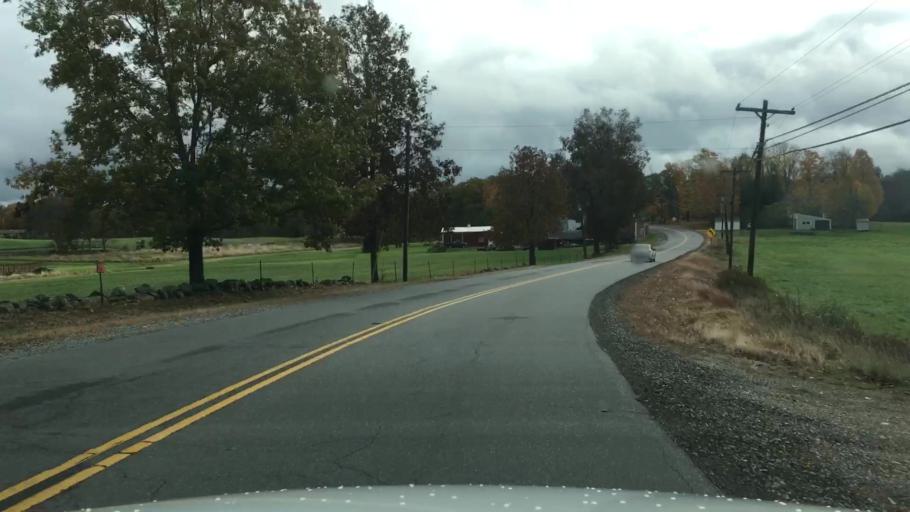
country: US
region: New Hampshire
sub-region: Strafford County
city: Lee
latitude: 43.1039
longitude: -70.9929
